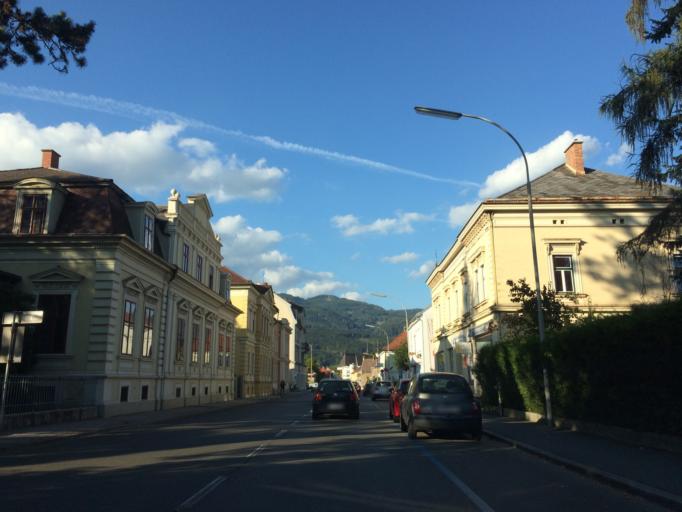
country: AT
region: Styria
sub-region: Politischer Bezirk Leoben
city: Leoben
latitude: 47.3748
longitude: 15.0908
